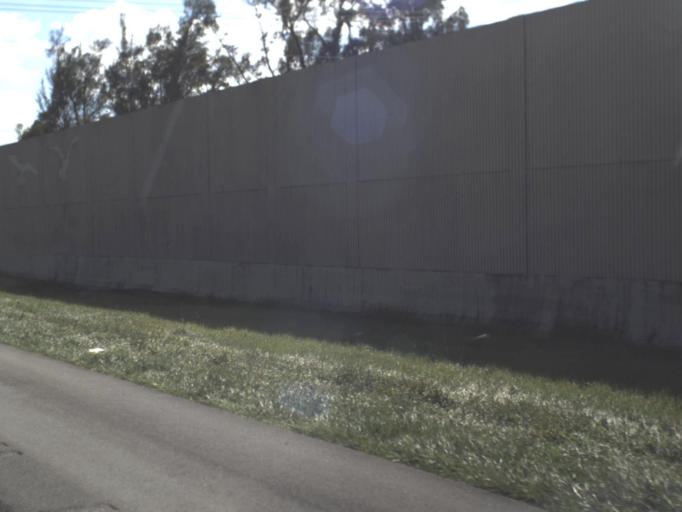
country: US
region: Florida
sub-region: Palm Beach County
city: Boca Del Mar
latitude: 26.3846
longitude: -80.1712
